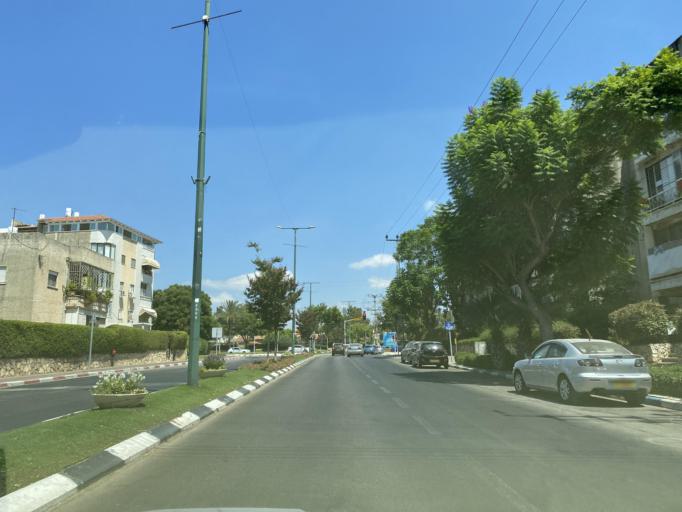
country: IL
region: Tel Aviv
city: Ramat HaSharon
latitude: 32.1676
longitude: 34.8518
